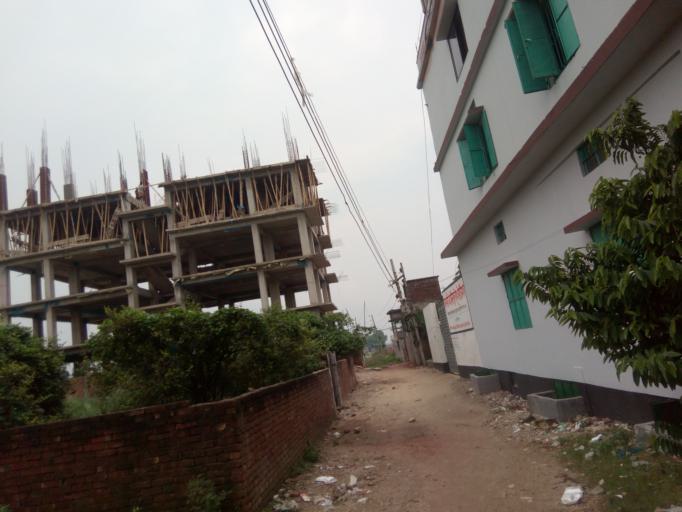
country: BD
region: Dhaka
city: Azimpur
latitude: 23.7409
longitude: 90.3528
